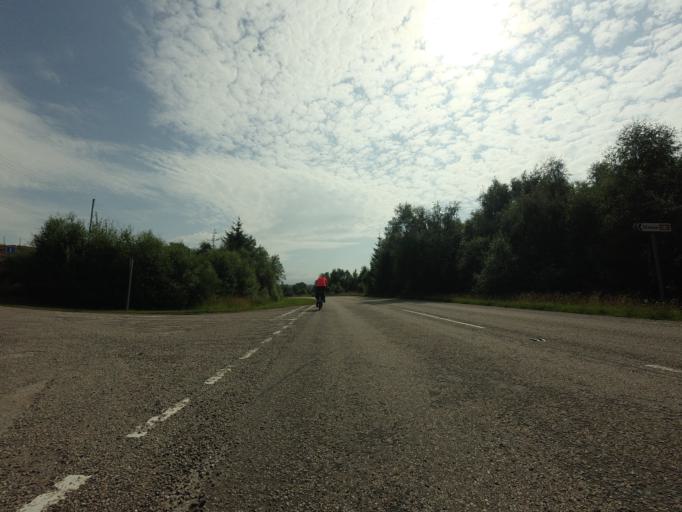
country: GB
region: Scotland
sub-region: Highland
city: Evanton
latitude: 57.9264
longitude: -4.4007
